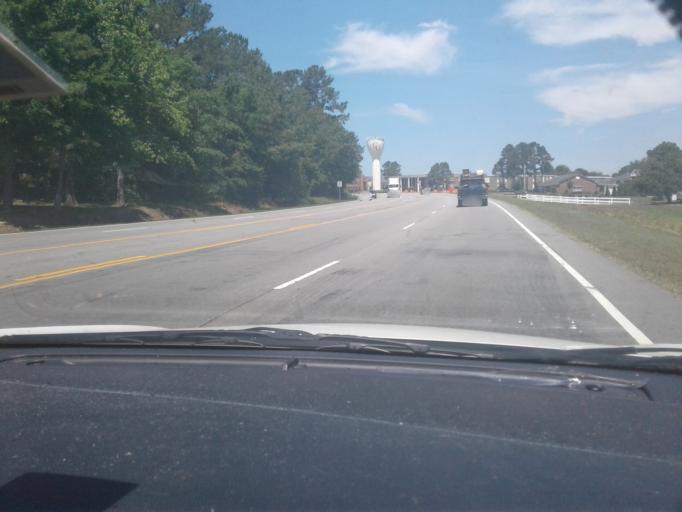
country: US
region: North Carolina
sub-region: Harnett County
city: Buies Creek
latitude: 35.4029
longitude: -78.7375
